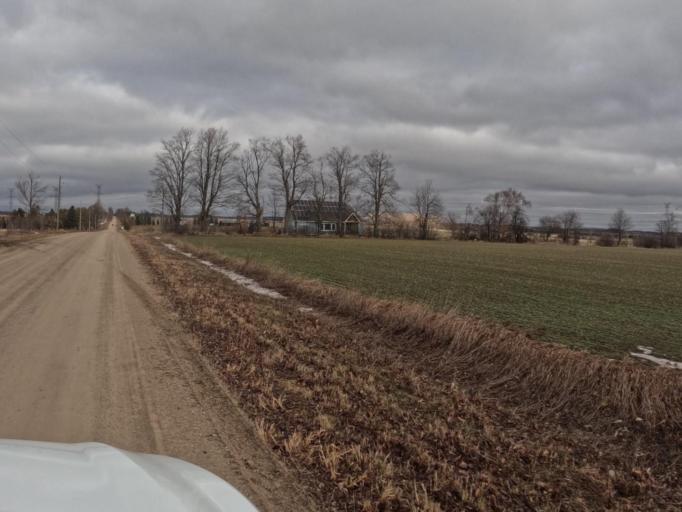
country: CA
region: Ontario
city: Shelburne
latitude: 43.9873
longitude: -80.4066
